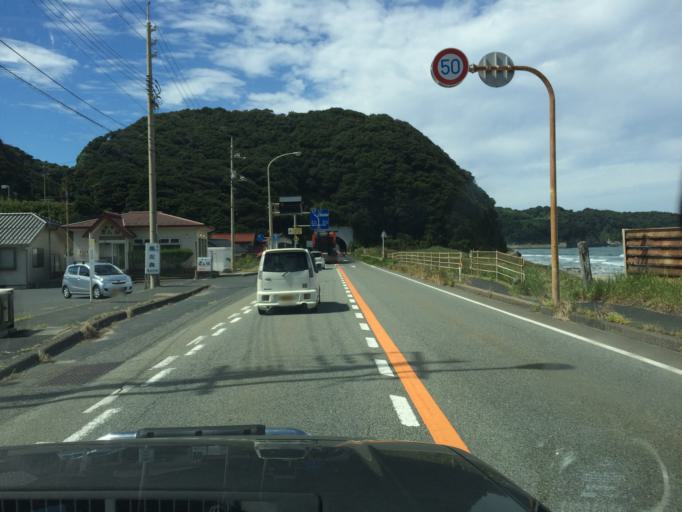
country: JP
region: Tottori
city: Tottori
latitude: 35.5179
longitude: 134.0312
